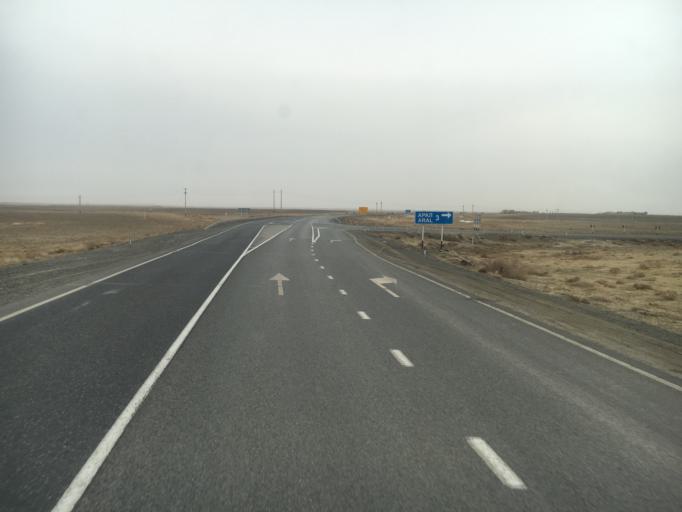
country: KZ
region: Qyzylorda
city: Aral
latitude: 46.8235
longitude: 61.7060
